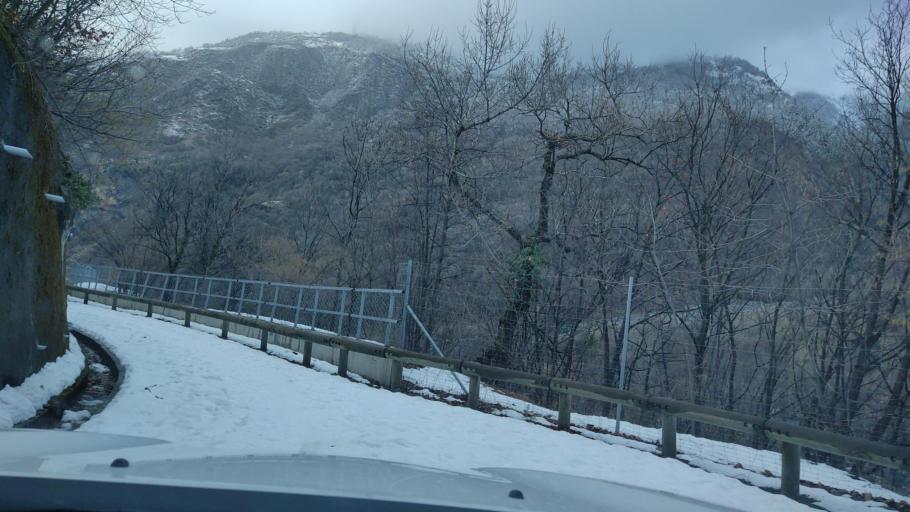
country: FR
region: Rhone-Alpes
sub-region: Departement de la Savoie
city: Saint-Michel-de-Maurienne
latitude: 45.2094
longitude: 6.5125
